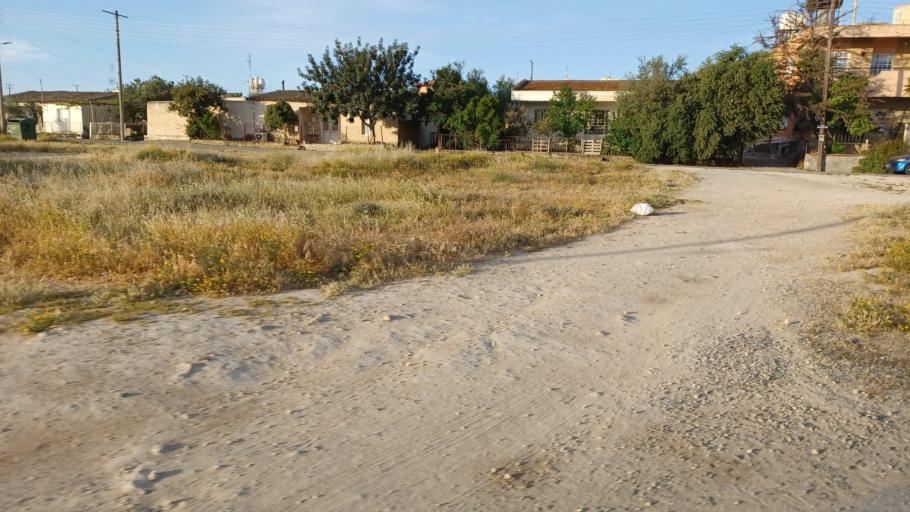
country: CY
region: Lefkosia
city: Akaki
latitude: 35.1667
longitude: 33.1454
